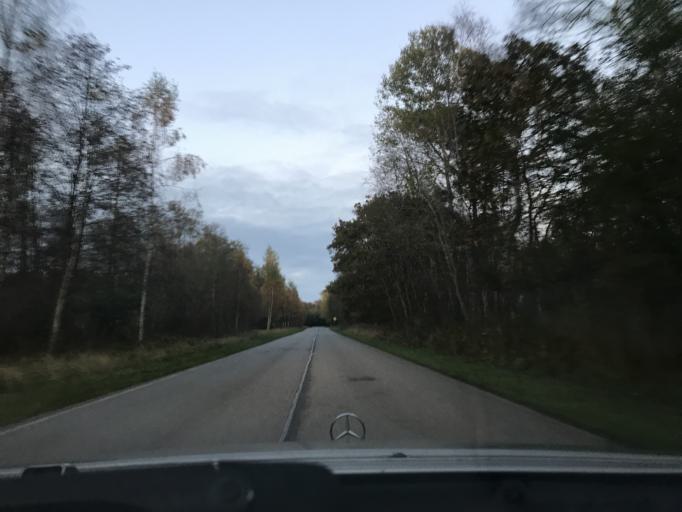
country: DE
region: Mecklenburg-Vorpommern
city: Karlshagen
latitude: 54.1502
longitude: 13.7951
